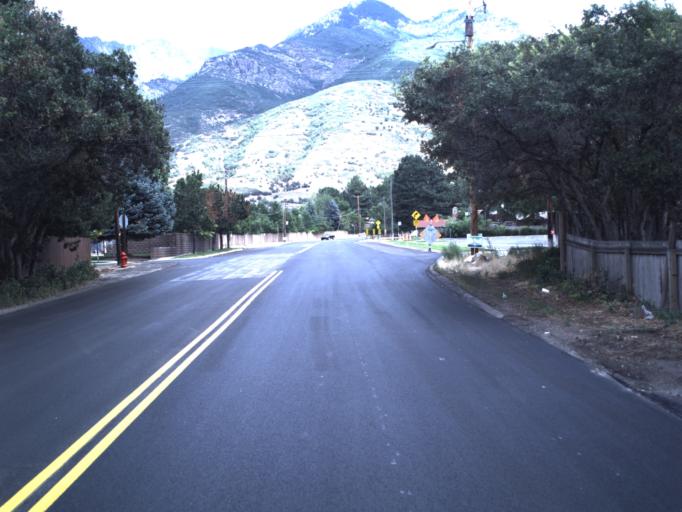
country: US
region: Utah
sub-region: Salt Lake County
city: Granite
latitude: 40.5777
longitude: -111.8062
